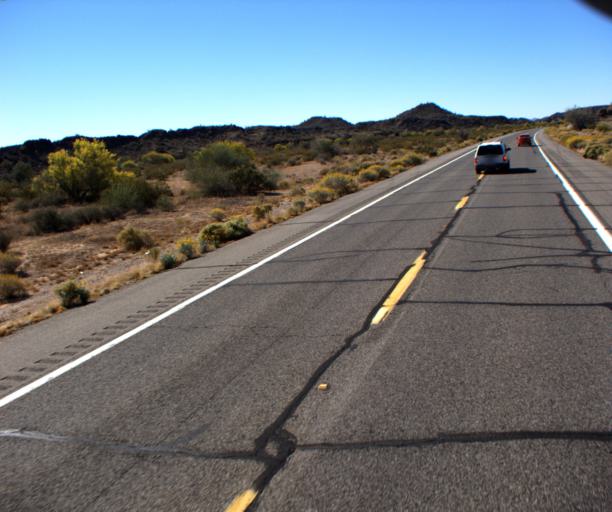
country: US
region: Arizona
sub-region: Pima County
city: Ajo
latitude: 32.5690
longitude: -112.8759
